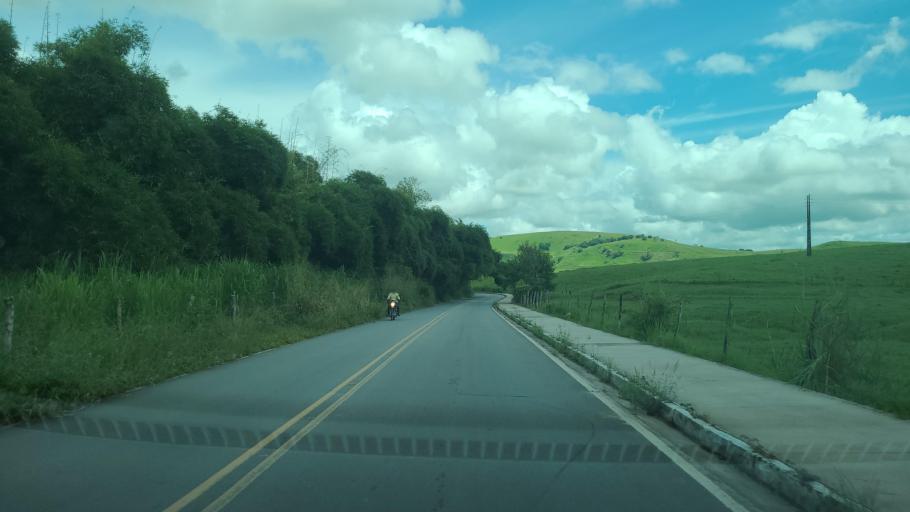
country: BR
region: Alagoas
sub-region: Uniao Dos Palmares
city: Uniao dos Palmares
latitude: -9.1567
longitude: -36.0391
